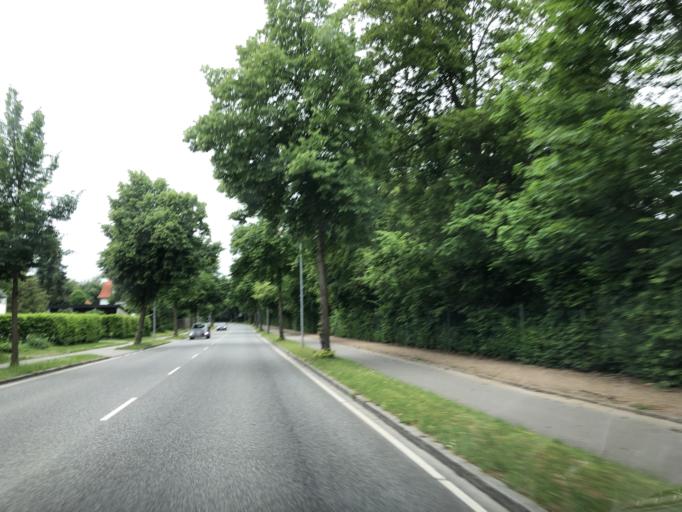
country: DK
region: Capital Region
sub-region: Lyngby-Tarbaek Kommune
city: Kongens Lyngby
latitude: 55.8059
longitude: 12.5059
